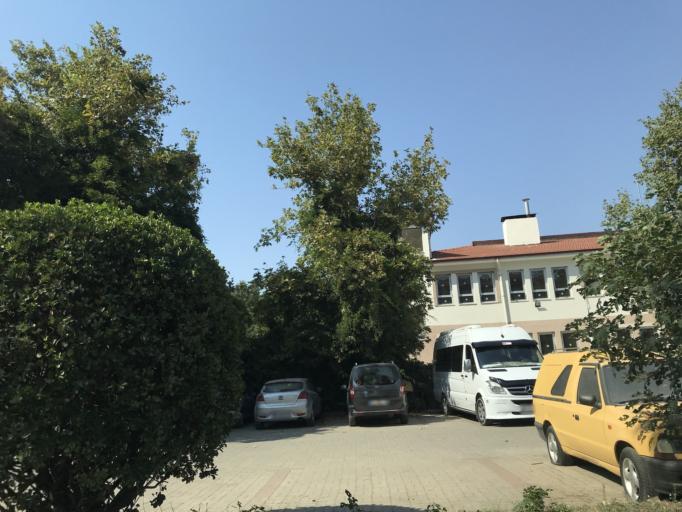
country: TR
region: Izmir
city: Selcuk
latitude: 37.9454
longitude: 27.3697
